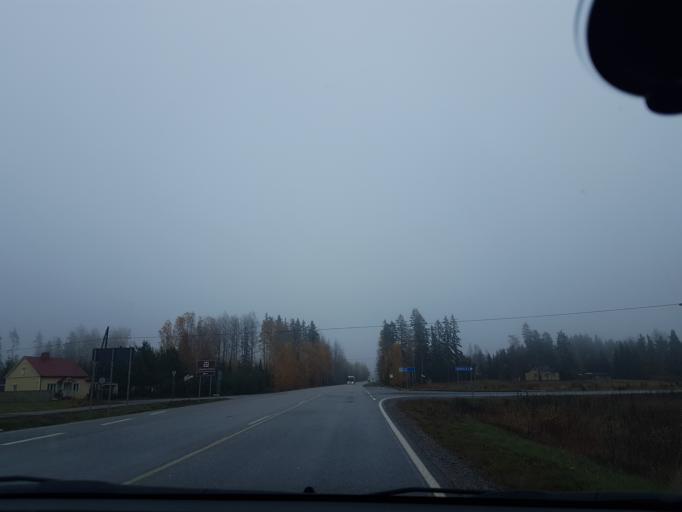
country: FI
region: Uusimaa
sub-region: Helsinki
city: Jaervenpaeae
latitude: 60.4702
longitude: 25.1512
